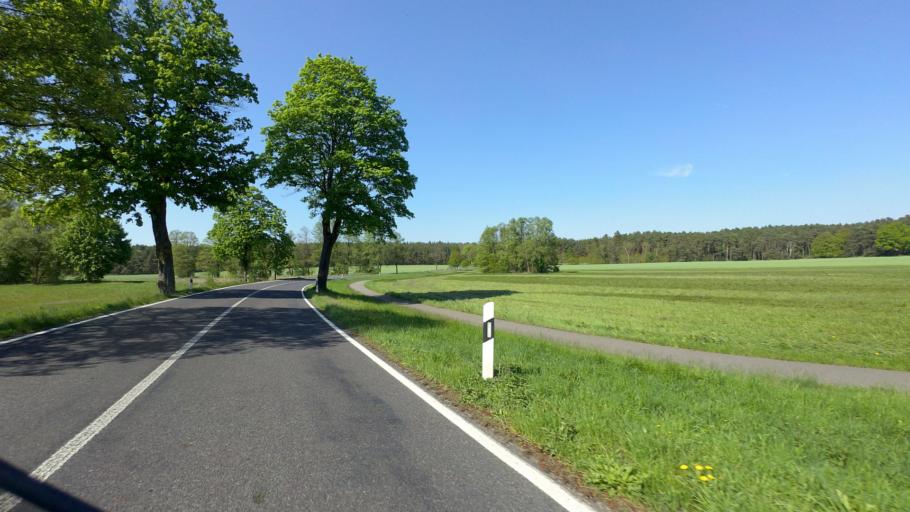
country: DE
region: Brandenburg
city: Neu Zauche
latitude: 52.0237
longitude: 14.0399
